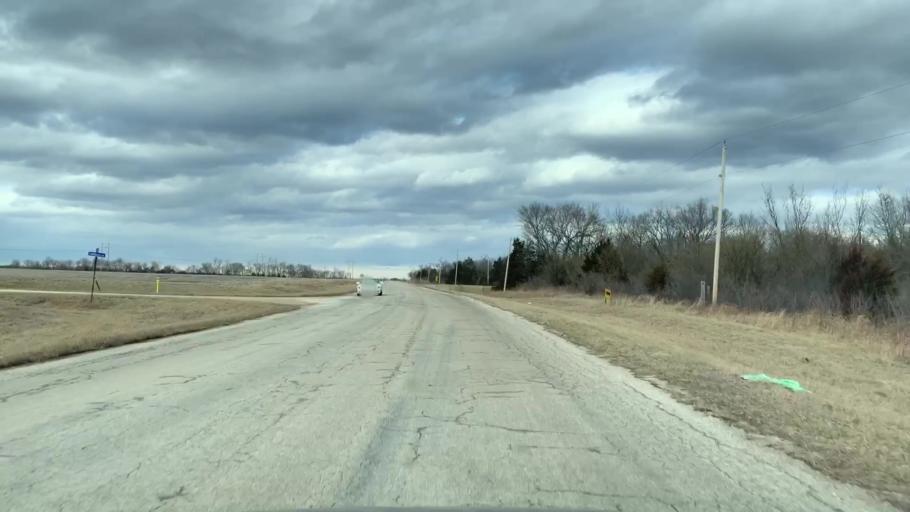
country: US
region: Kansas
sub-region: Allen County
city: Humboldt
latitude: 37.7617
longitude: -95.4707
